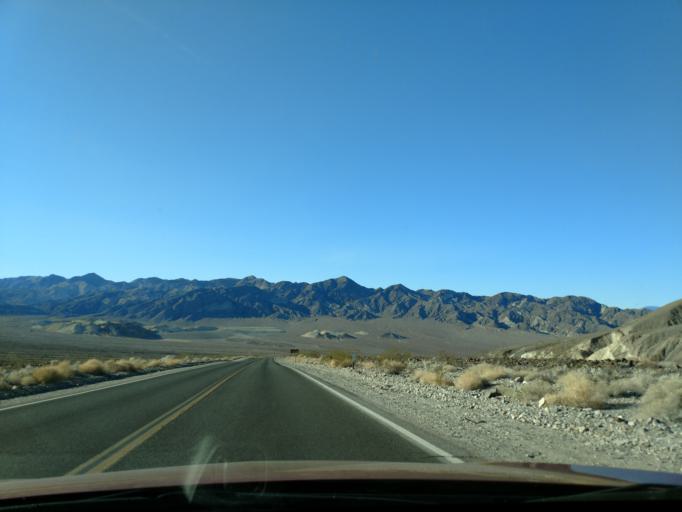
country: US
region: Nevada
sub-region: Nye County
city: Beatty
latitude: 36.3733
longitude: -116.6943
